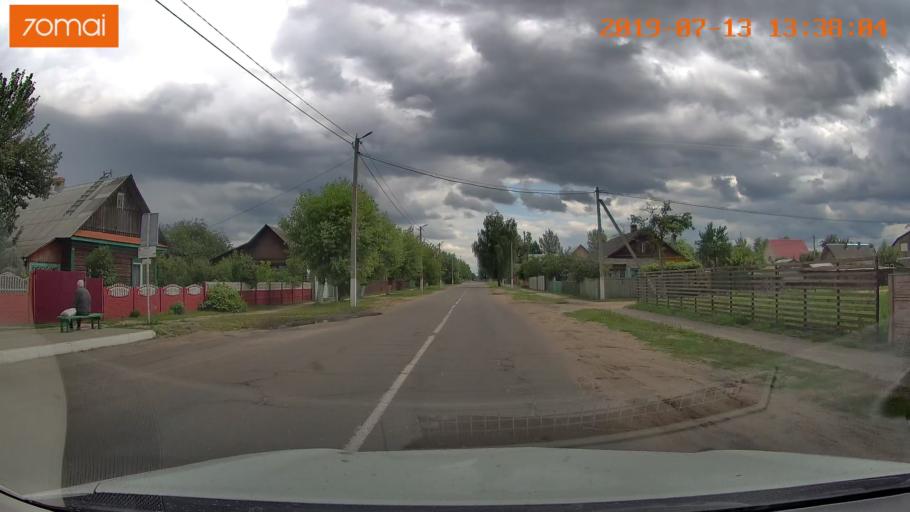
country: BY
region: Mogilev
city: Asipovichy
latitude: 53.2991
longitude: 28.6310
